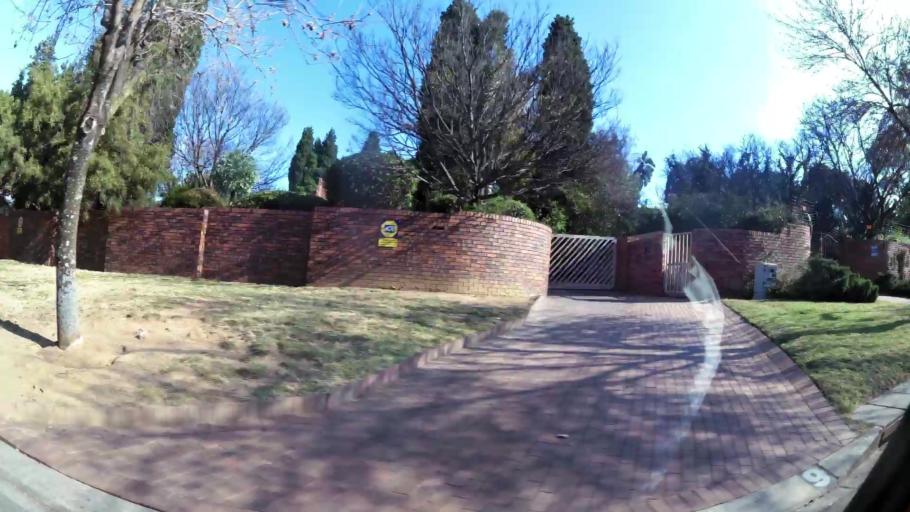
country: ZA
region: Gauteng
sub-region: City of Johannesburg Metropolitan Municipality
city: Roodepoort
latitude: -26.1002
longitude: 27.9492
